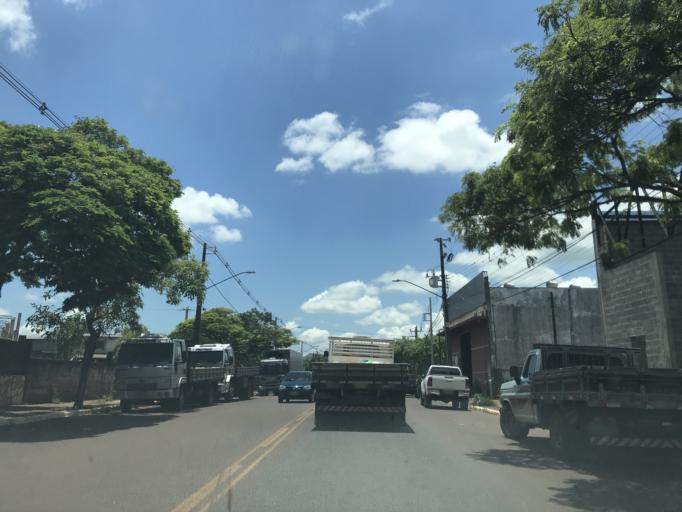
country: BR
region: Parana
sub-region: Marialva
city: Marialva
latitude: -23.4911
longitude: -51.7862
